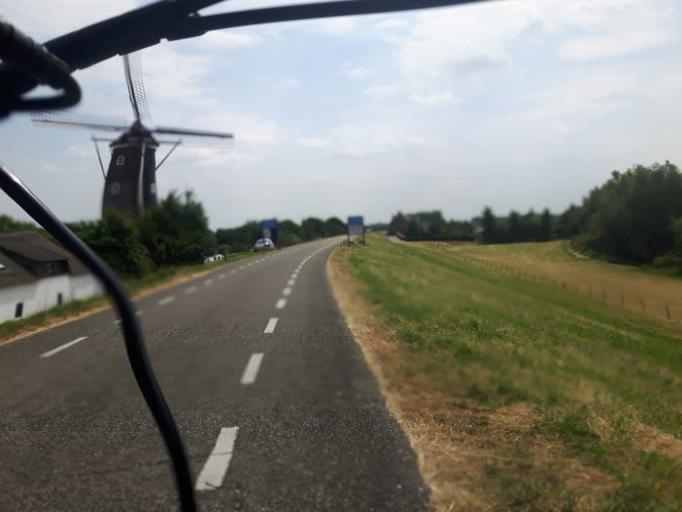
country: NL
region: Gelderland
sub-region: Gemeente Zaltbommel
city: Zaltbommel
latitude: 51.8145
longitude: 5.2094
